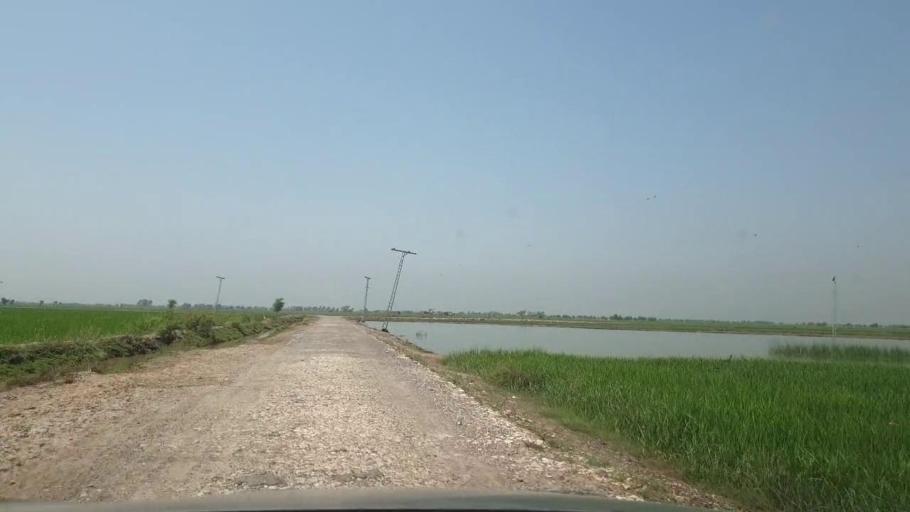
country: PK
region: Sindh
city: Warah
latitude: 27.4877
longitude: 67.7806
